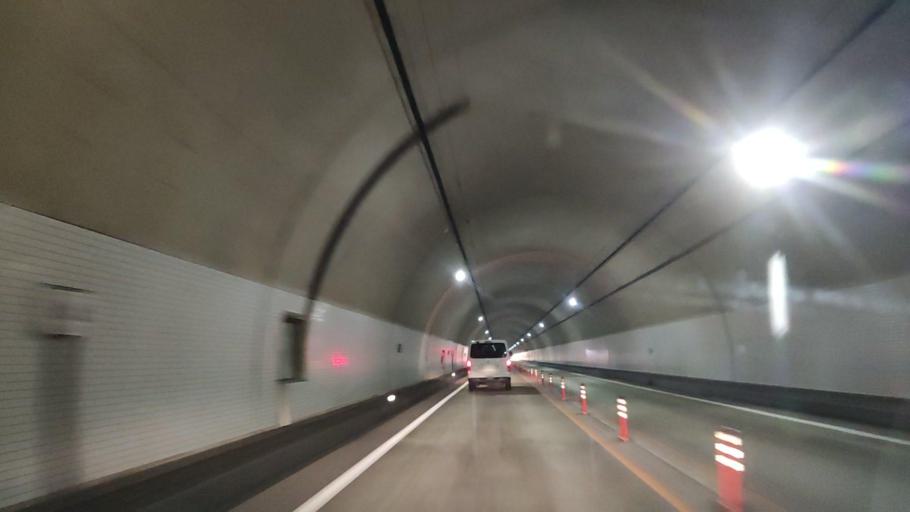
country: JP
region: Akita
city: Odate
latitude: 40.3425
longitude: 140.6500
